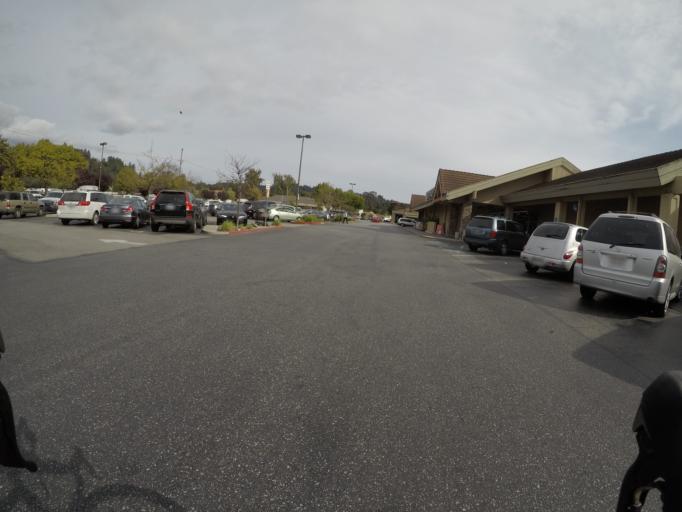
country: US
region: California
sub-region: Santa Cruz County
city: Scotts Valley
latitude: 37.0467
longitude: -122.0313
